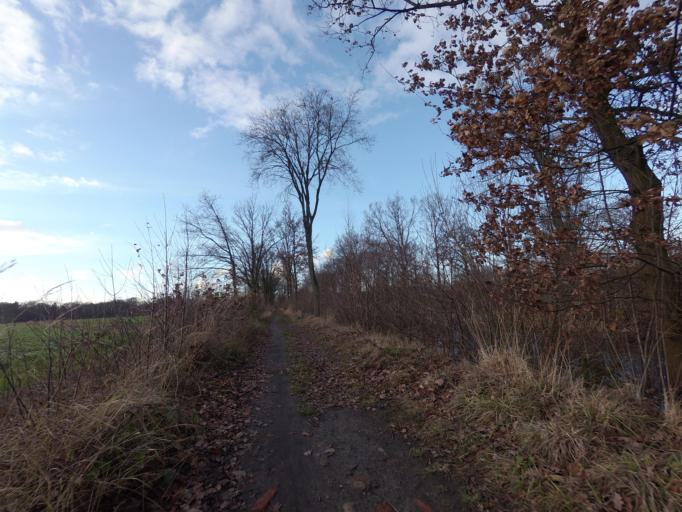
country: BE
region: Flanders
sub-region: Provincie Antwerpen
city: Kapellen
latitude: 51.3466
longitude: 4.4118
